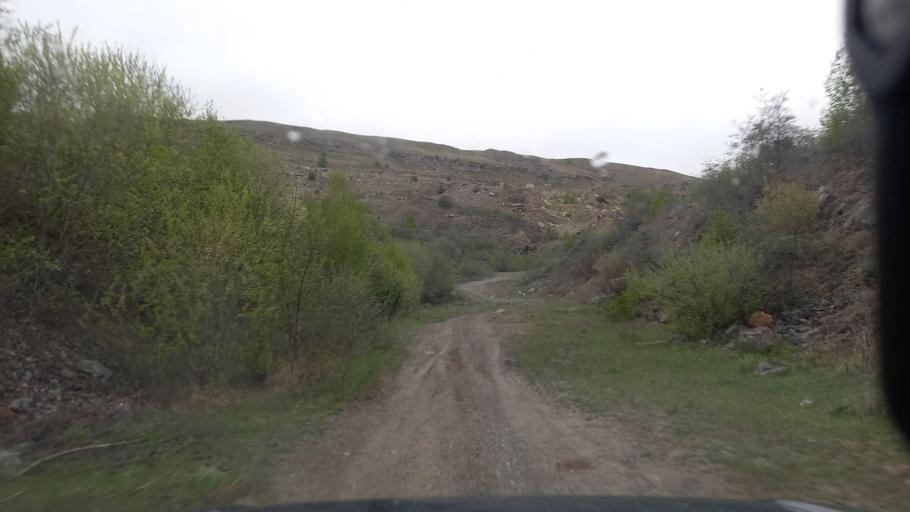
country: RU
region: Kabardino-Balkariya
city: Bylym
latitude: 43.4569
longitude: 42.9989
